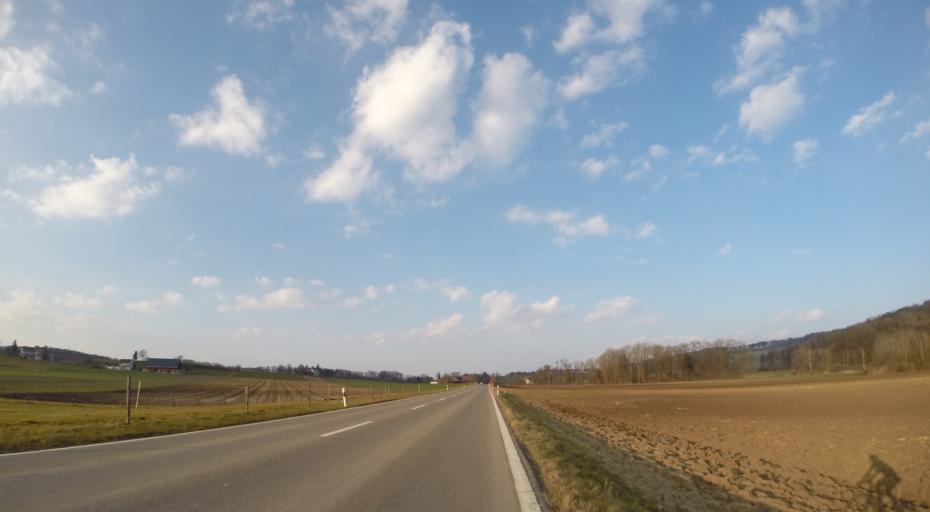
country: CH
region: Thurgau
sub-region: Frauenfeld District
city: Steckborn
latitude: 47.6405
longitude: 8.9762
